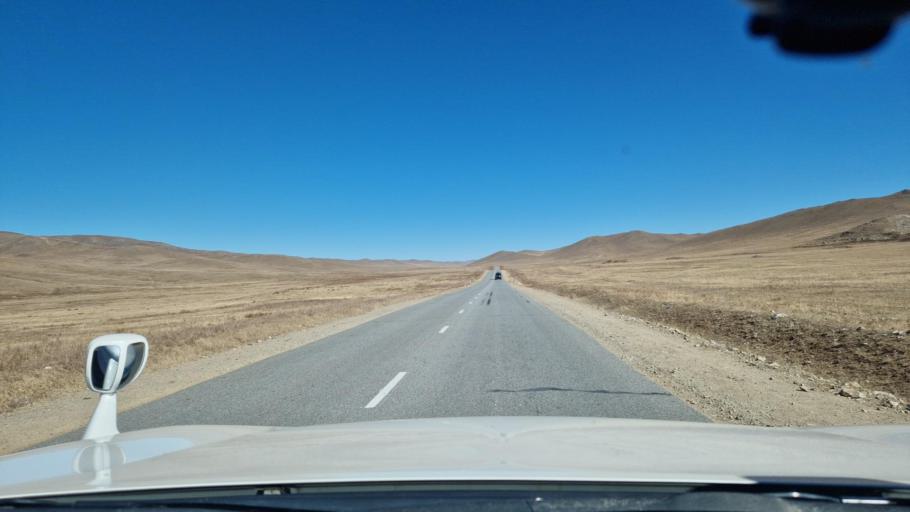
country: MN
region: Central Aimak
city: Bayandelger
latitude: 47.6995
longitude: 108.5557
